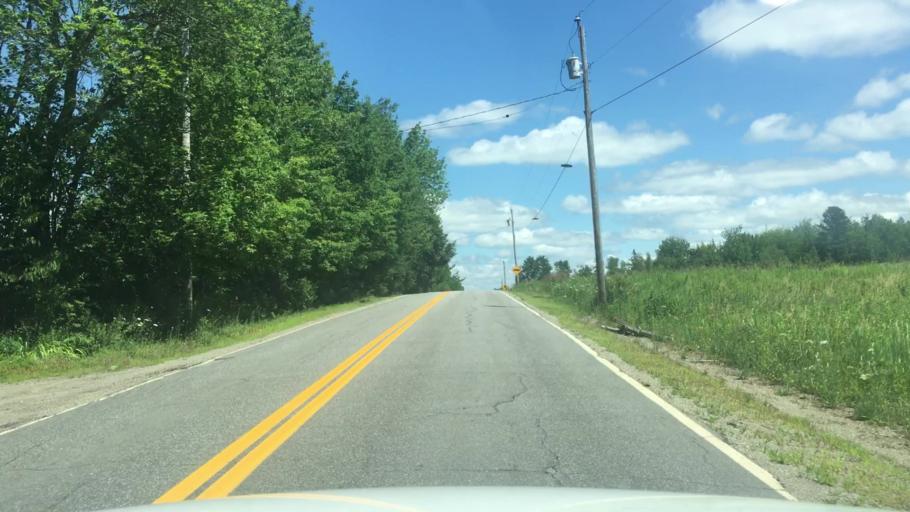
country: US
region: Maine
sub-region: Waldo County
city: Searsmont
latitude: 44.4063
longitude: -69.3239
